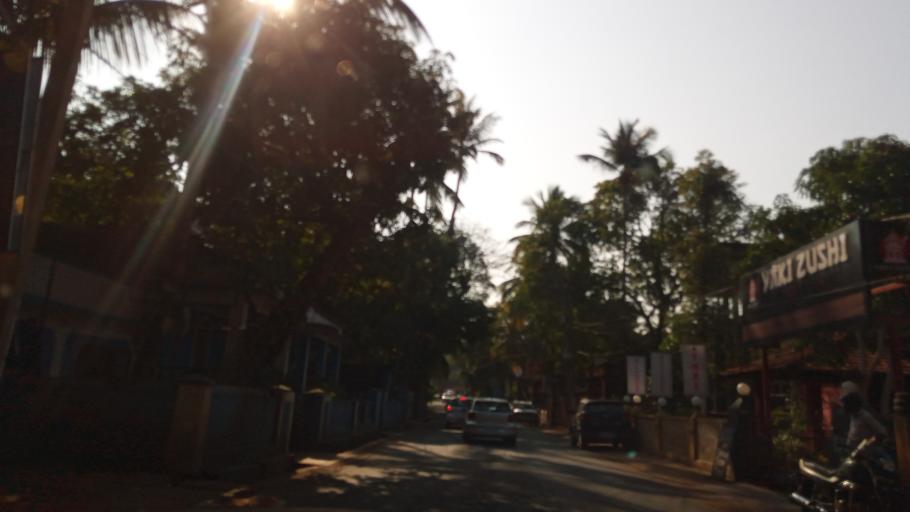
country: IN
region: Goa
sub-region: North Goa
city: Saligao
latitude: 15.5435
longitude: 73.8132
